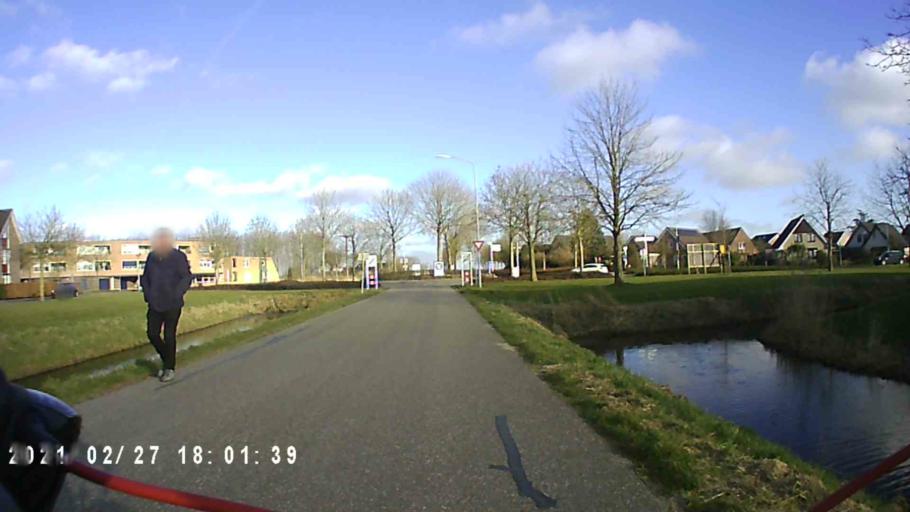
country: NL
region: Groningen
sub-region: Gemeente Bedum
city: Bedum
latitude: 53.3016
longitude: 6.6109
